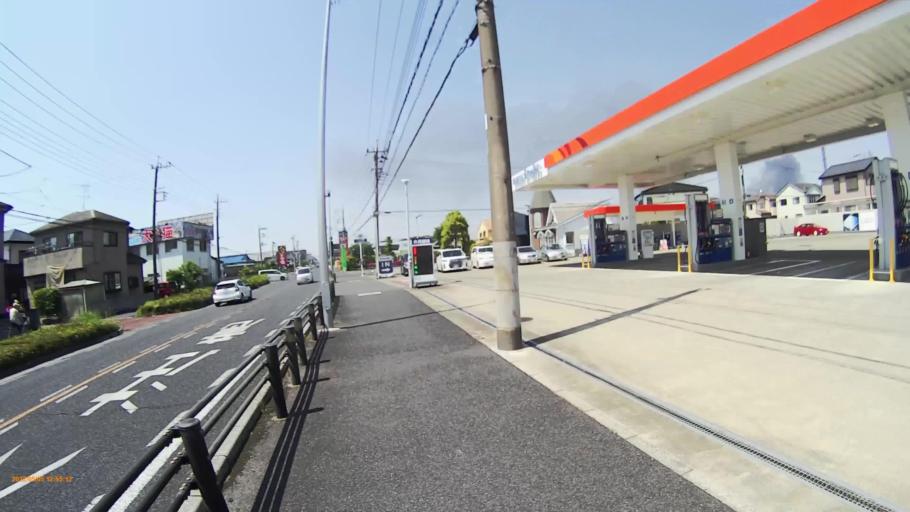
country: JP
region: Saitama
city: Kasukabe
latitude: 35.9563
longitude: 139.7765
